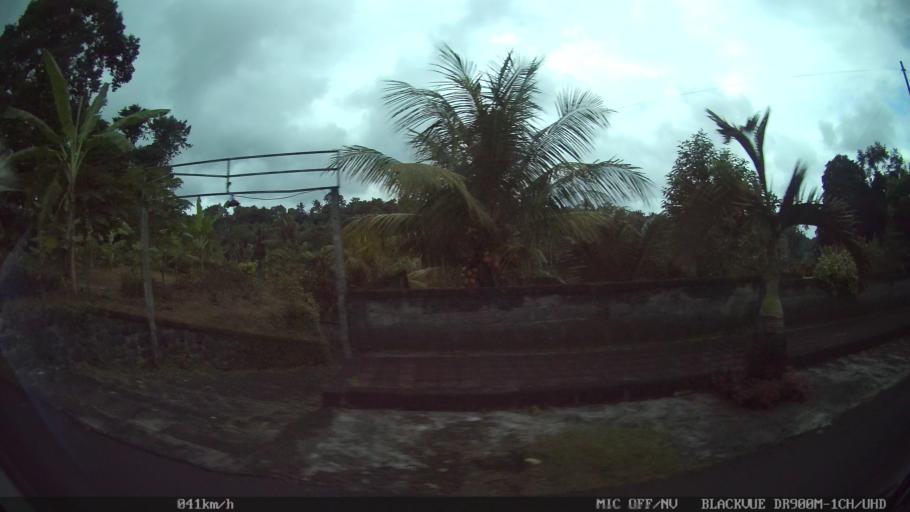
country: ID
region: Bali
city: Banjar Cemenggon
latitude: -8.5347
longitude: 115.1923
